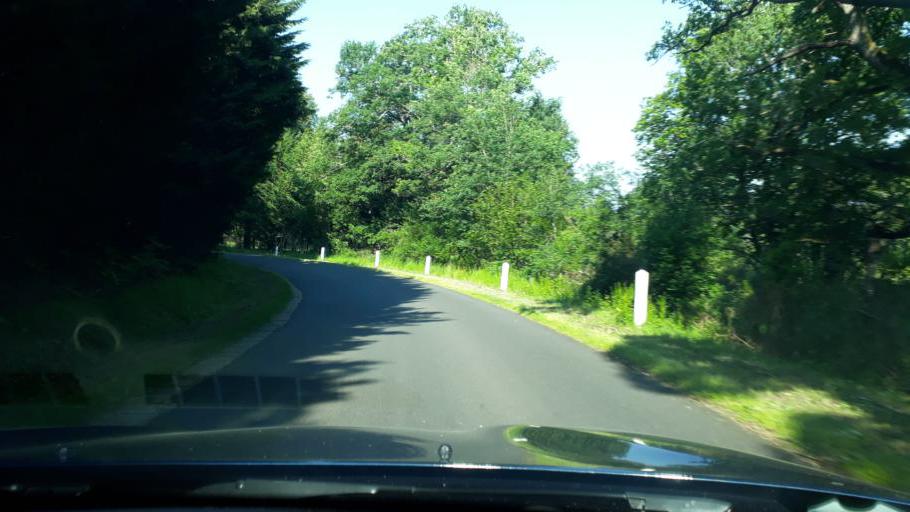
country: FR
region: Centre
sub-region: Departement du Loir-et-Cher
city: Dhuizon
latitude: 47.6253
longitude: 1.7137
